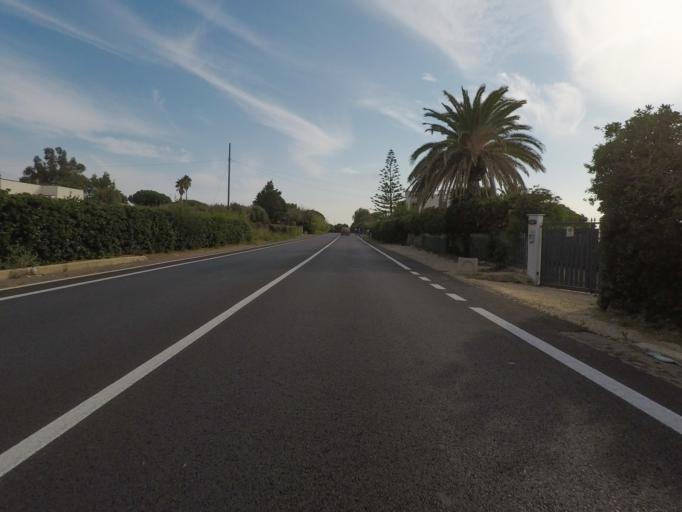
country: IT
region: Latium
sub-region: Citta metropolitana di Roma Capitale
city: Civitavecchia
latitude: 42.0501
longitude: 11.8205
